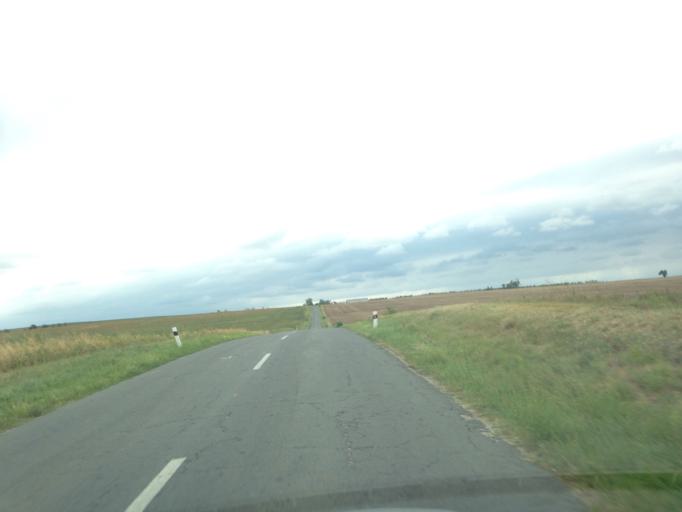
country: SK
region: Nitriansky
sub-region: Okres Komarno
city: Hurbanovo
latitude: 47.9065
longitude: 18.2839
